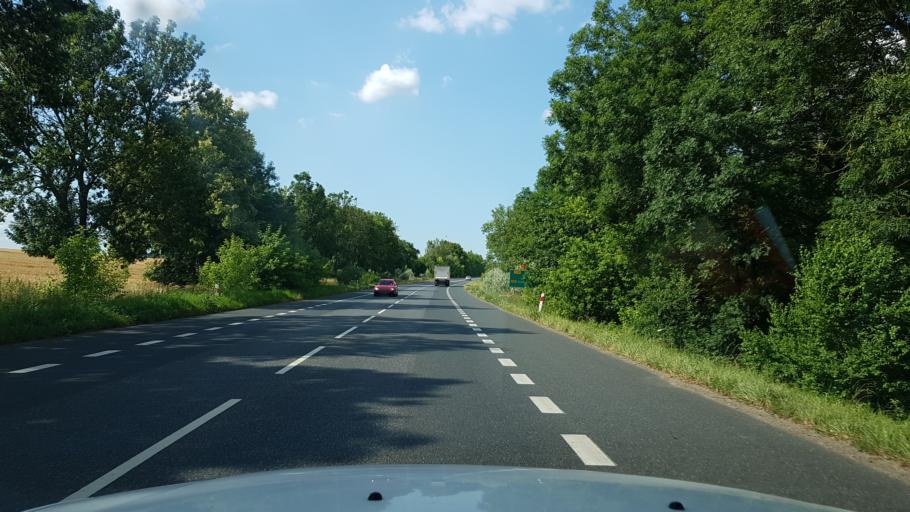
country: PL
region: West Pomeranian Voivodeship
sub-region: Powiat gryfinski
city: Stare Czarnowo
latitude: 53.2707
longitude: 14.7818
